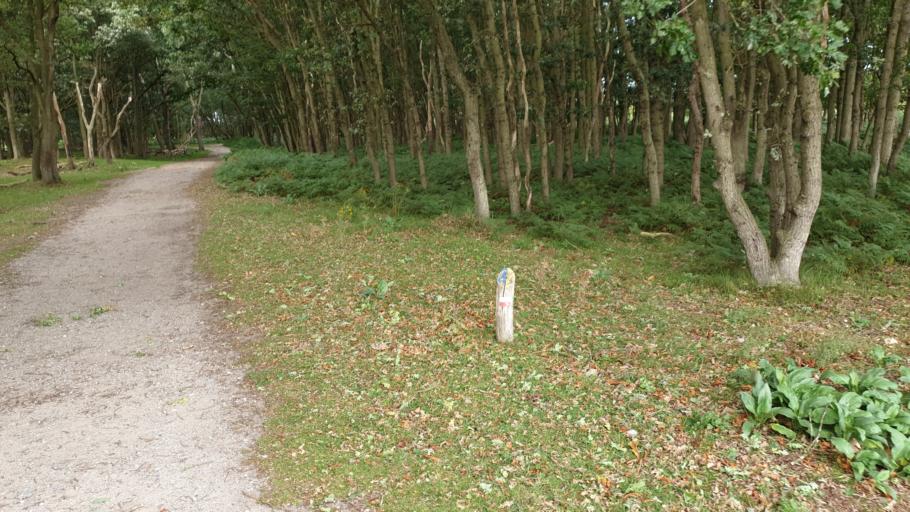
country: NL
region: South Holland
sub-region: Gemeente Lisse
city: Lisse
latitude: 52.3025
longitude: 4.5303
